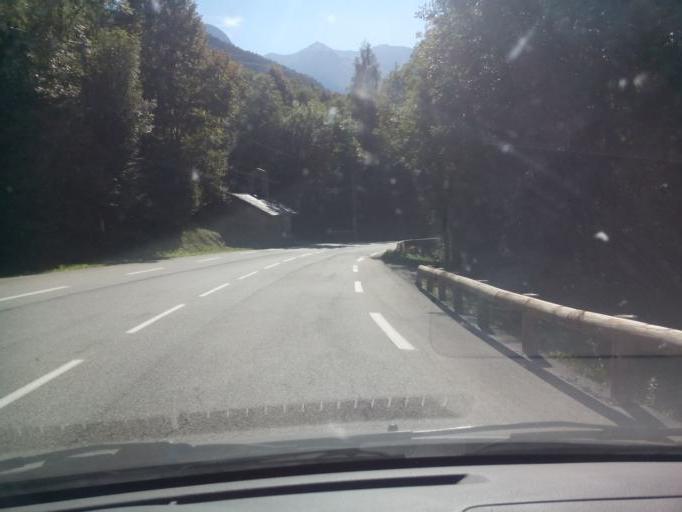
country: FR
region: Rhone-Alpes
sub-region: Departement de l'Isere
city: Les Deux Alpes
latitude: 45.0327
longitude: 6.0902
